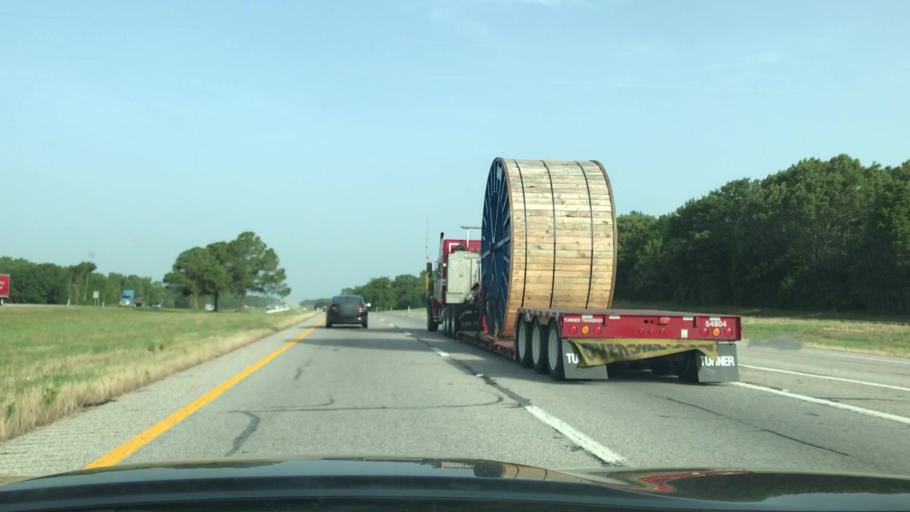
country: US
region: Texas
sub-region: Van Zandt County
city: Van
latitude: 32.5280
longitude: -95.7168
